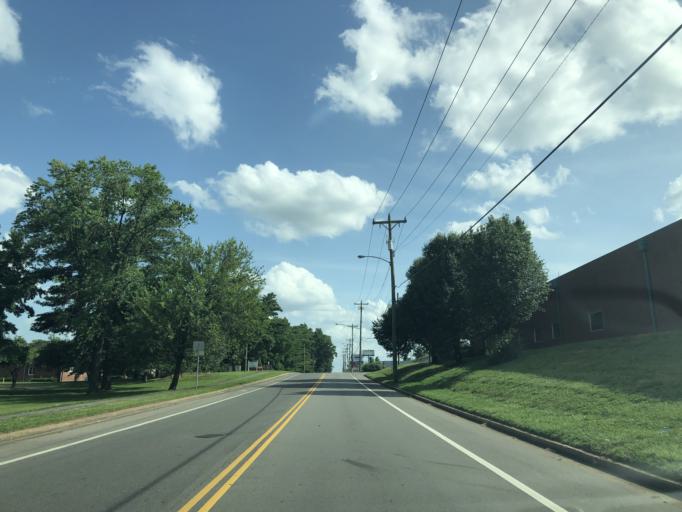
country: US
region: Tennessee
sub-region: Davidson County
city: Nashville
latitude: 36.1359
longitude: -86.7412
